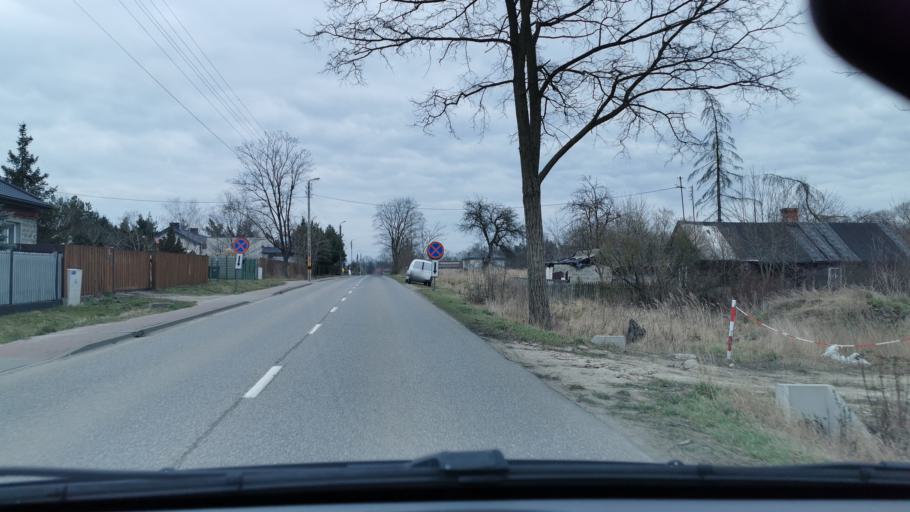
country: PL
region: Masovian Voivodeship
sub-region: Powiat zyrardowski
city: Radziejowice
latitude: 52.0112
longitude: 20.5249
